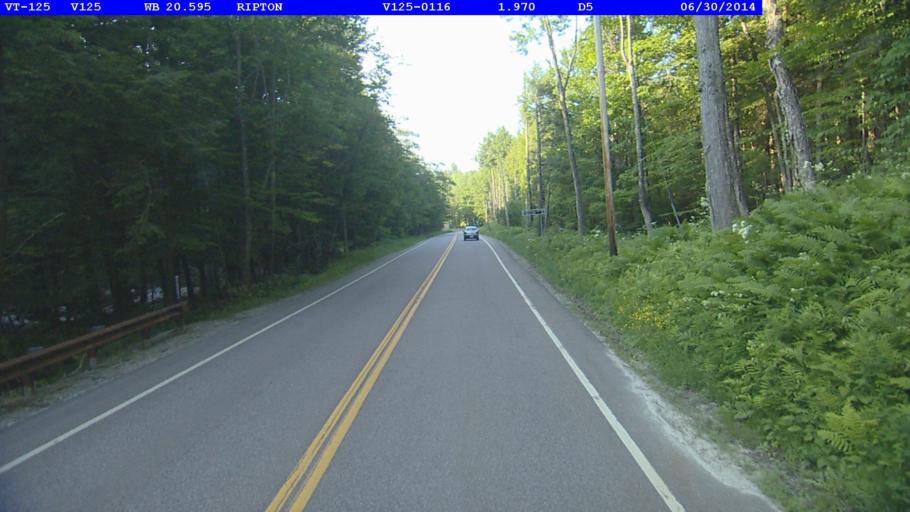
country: US
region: Vermont
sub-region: Addison County
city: Middlebury (village)
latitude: 43.9678
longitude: -73.0302
